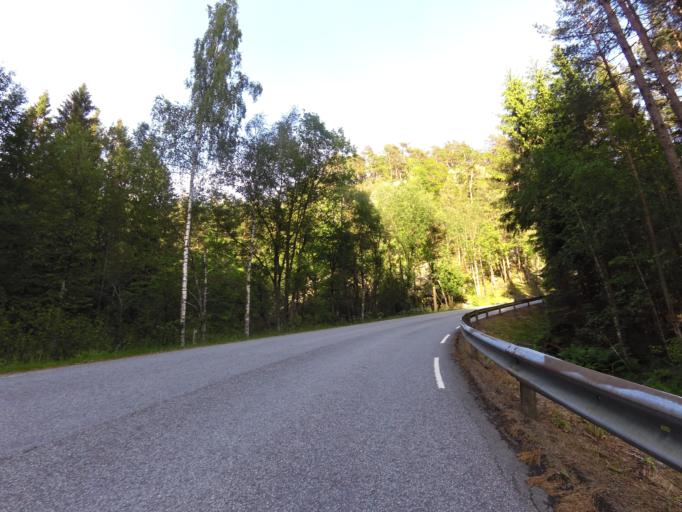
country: NO
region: Vest-Agder
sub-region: Flekkefjord
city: Flekkefjord
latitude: 58.2793
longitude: 6.6352
